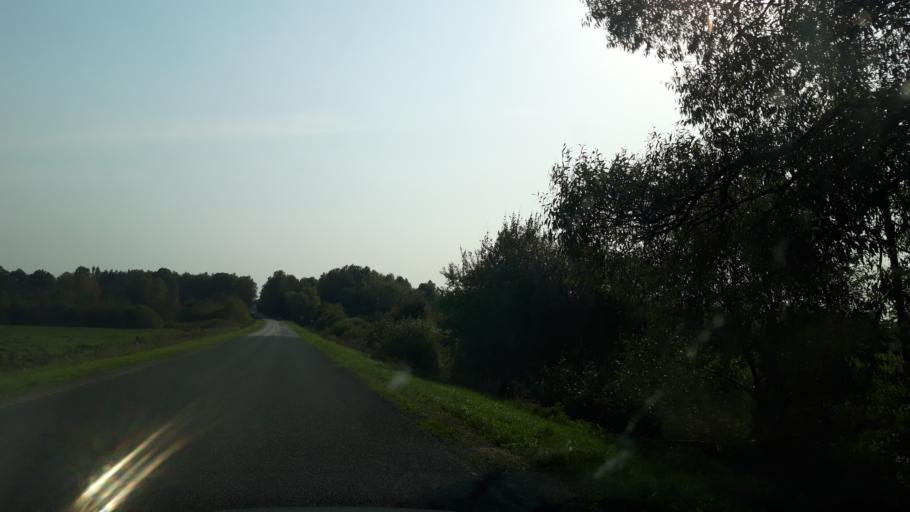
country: LV
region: Burtnieki
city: Matisi
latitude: 57.6573
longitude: 25.2284
